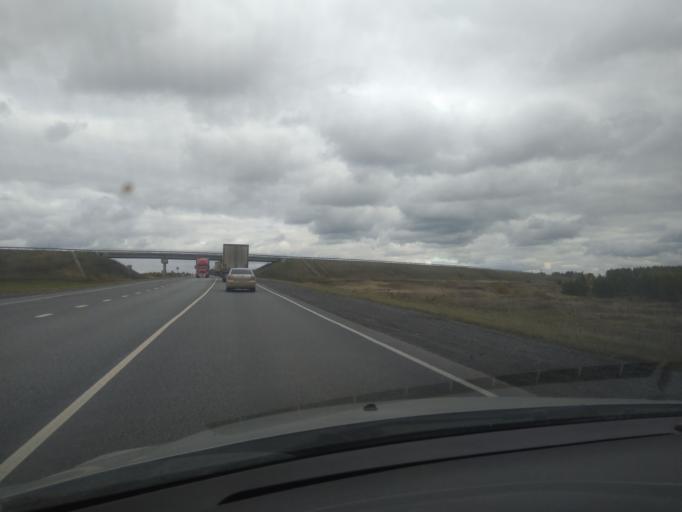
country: RU
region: Sverdlovsk
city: Yelanskiy
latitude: 56.7844
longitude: 62.4997
